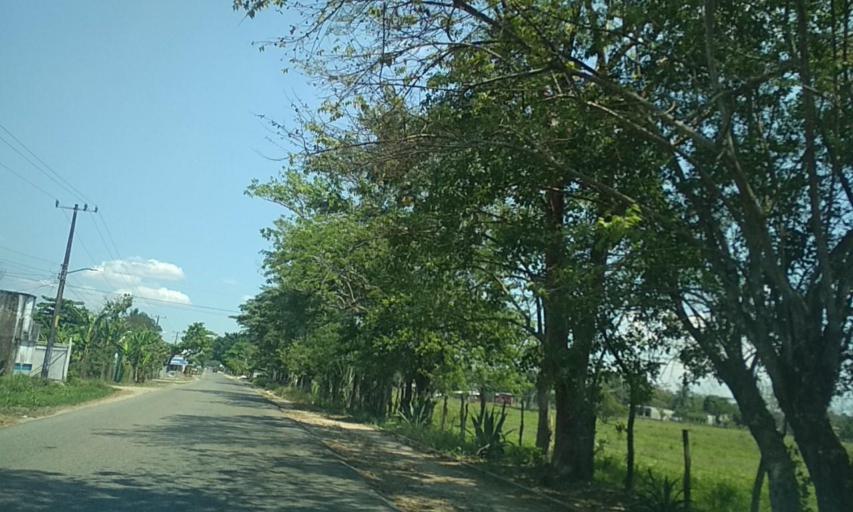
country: MX
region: Tabasco
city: Huimanguillo
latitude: 17.7939
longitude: -93.4453
